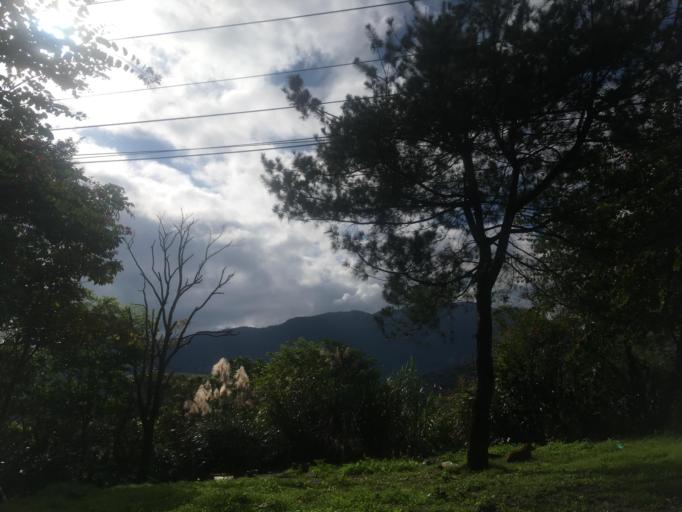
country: TW
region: Taiwan
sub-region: Yilan
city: Yilan
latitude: 24.6486
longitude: 121.5738
